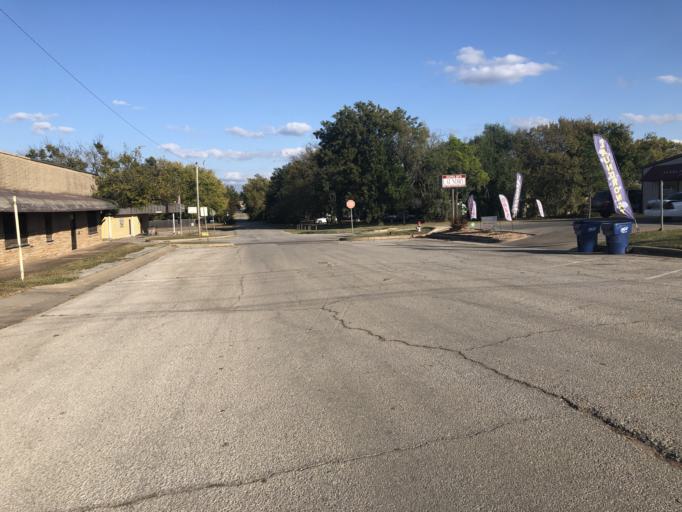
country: US
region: Oklahoma
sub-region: Pottawatomie County
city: Tecumseh
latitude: 35.2587
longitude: -96.9360
